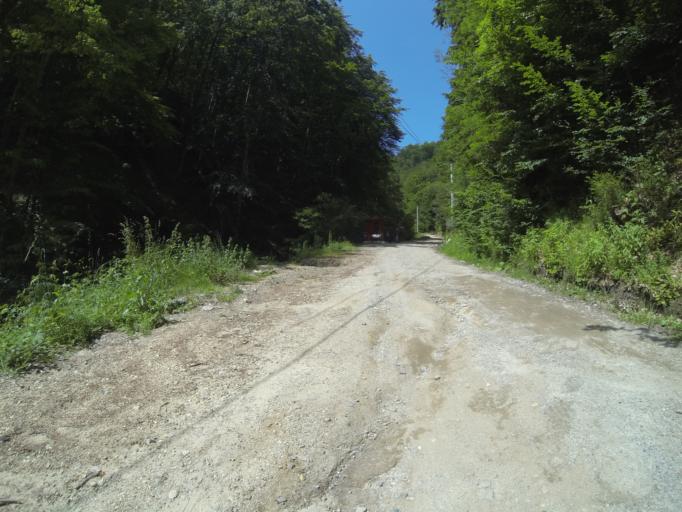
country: RO
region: Valcea
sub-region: Oras Baile Olanesti
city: Baile Olanesti
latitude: 45.2116
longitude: 24.2192
